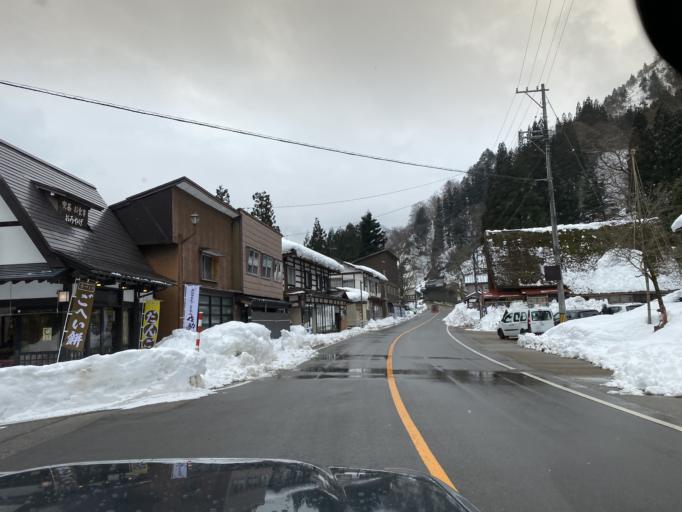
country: JP
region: Toyama
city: Fukumitsu
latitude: 36.4104
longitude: 136.9311
